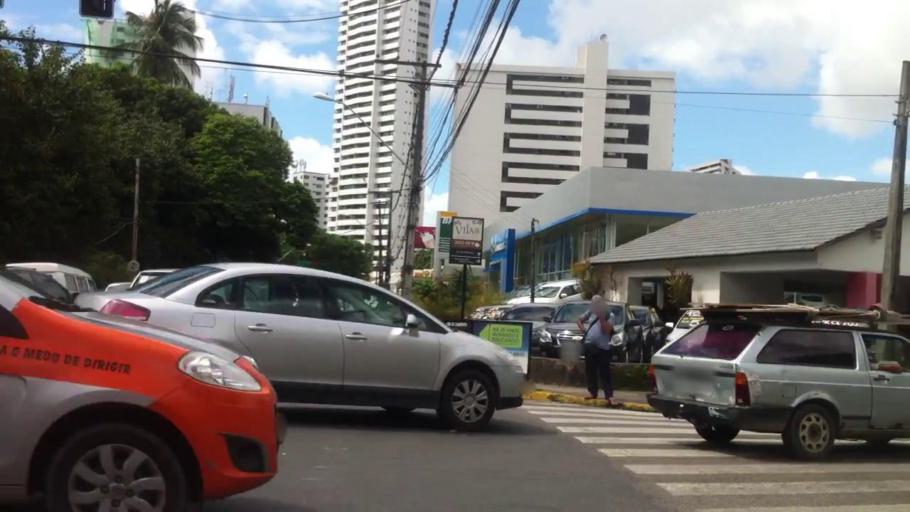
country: BR
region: Pernambuco
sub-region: Recife
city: Recife
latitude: -8.0443
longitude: -34.9022
